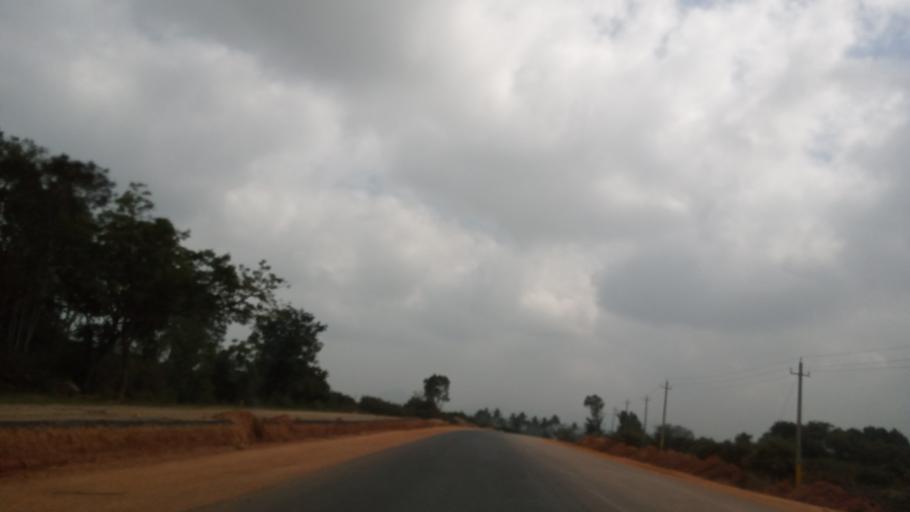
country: IN
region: Karnataka
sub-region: Kolar
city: Srinivaspur
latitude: 13.4472
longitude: 78.2429
